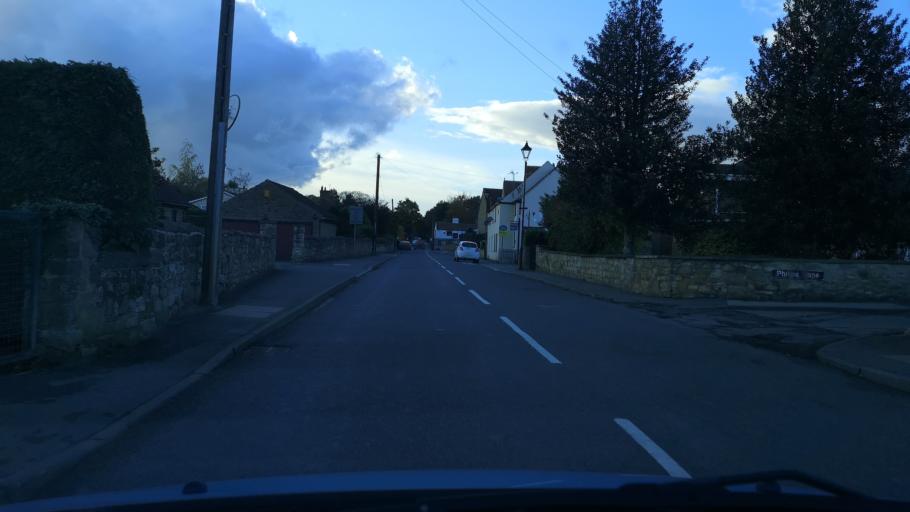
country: GB
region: England
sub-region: City and Borough of Wakefield
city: Darrington
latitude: 53.6747
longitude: -1.2678
